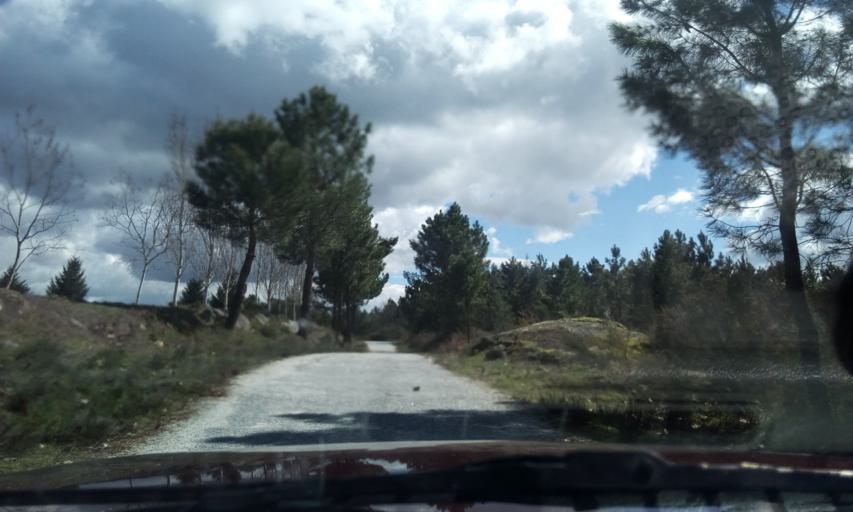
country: PT
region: Guarda
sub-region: Fornos de Algodres
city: Fornos de Algodres
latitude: 40.6674
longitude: -7.5021
